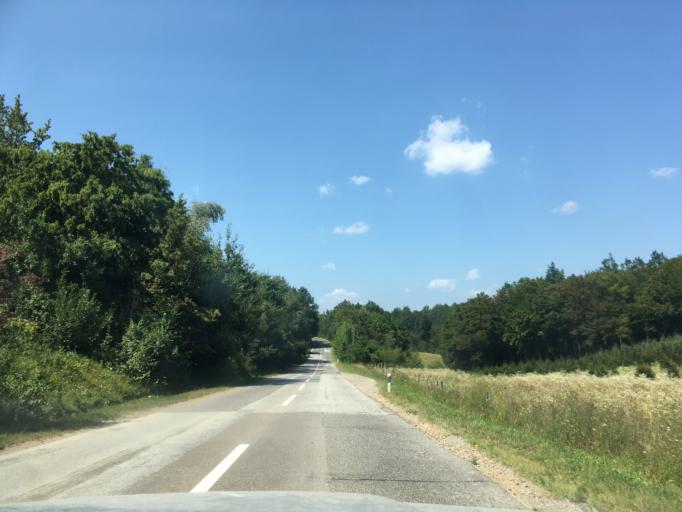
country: HR
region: Karlovacka
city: Ozalj
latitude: 45.5188
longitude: 15.3941
